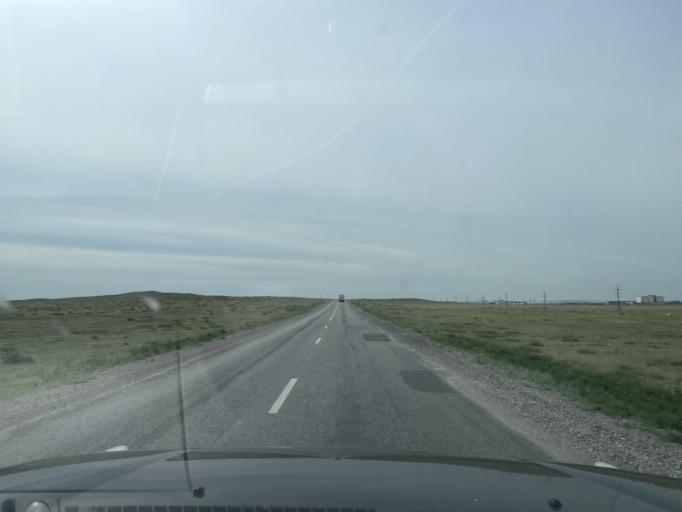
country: KZ
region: Qaraghandy
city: Abay
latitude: 49.3856
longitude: 72.9166
